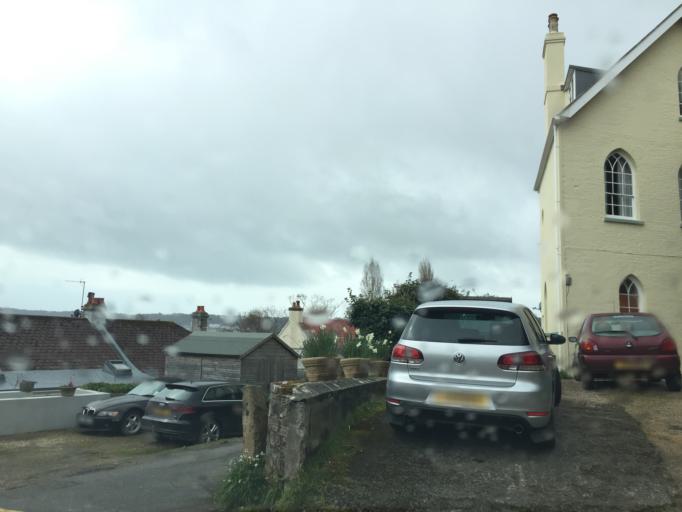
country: JE
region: St Helier
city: Saint Helier
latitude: 49.2021
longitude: -2.1530
